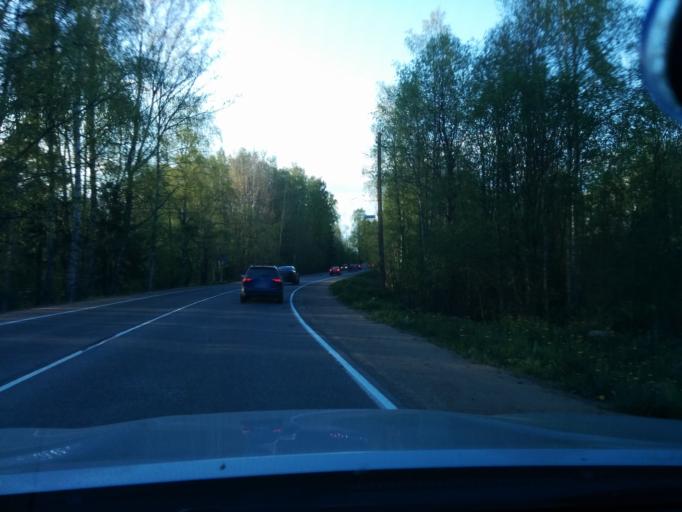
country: RU
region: Leningrad
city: Verkhniye Osel'ki
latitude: 60.2296
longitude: 30.4321
